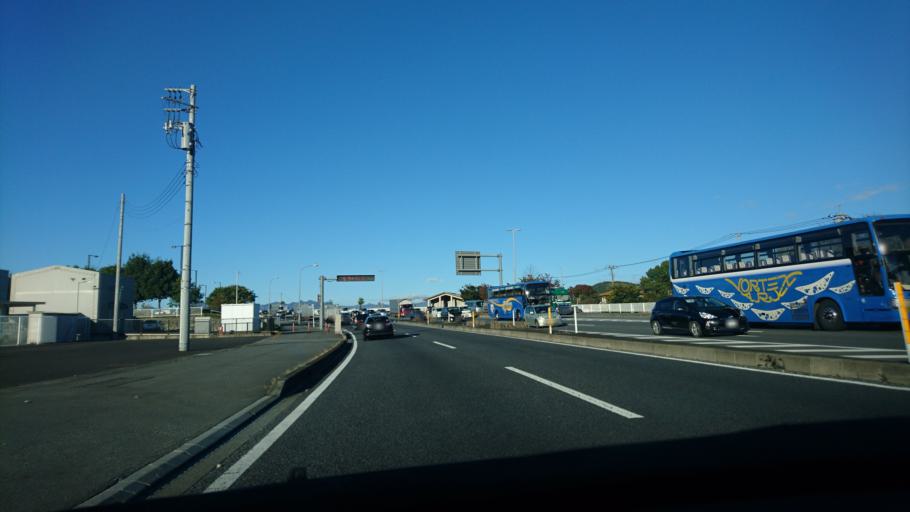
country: JP
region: Gunma
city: Annaka
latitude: 36.3358
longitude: 138.9405
